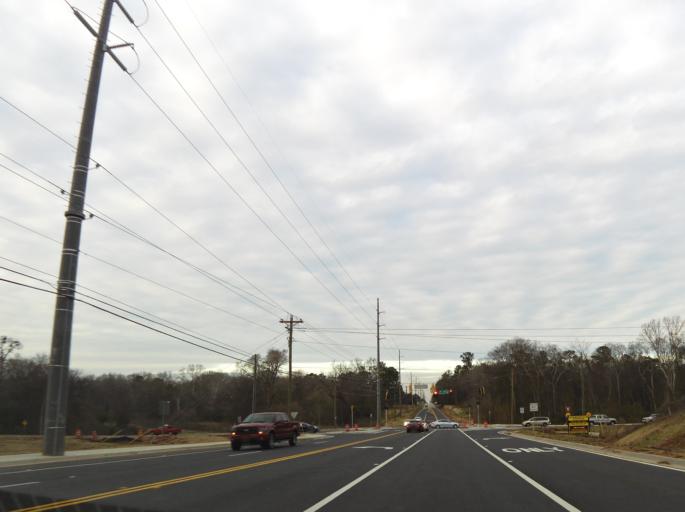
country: US
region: Georgia
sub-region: Houston County
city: Centerville
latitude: 32.6324
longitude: -83.7090
